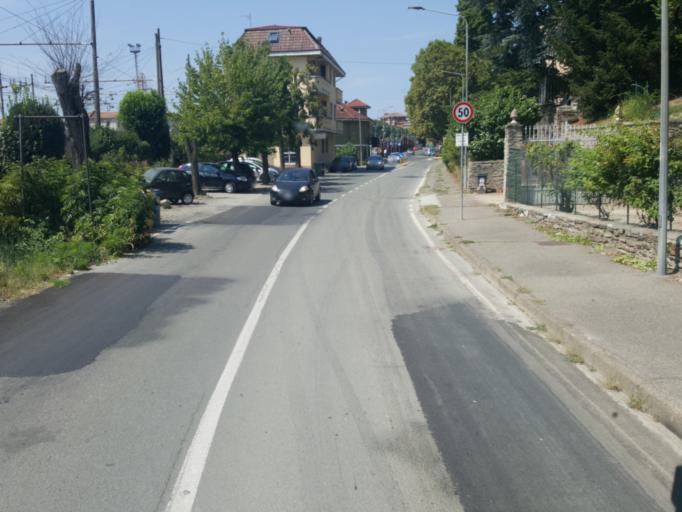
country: IT
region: Piedmont
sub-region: Provincia di Alessandria
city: Acqui Terme
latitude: 44.6730
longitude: 8.4791
